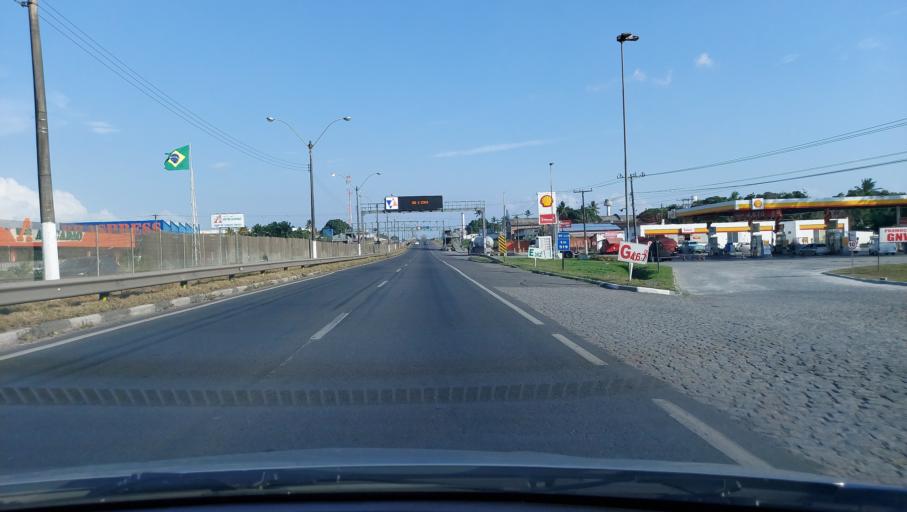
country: BR
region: Bahia
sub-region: Feira De Santana
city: Feira de Santana
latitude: -12.2778
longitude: -38.9283
